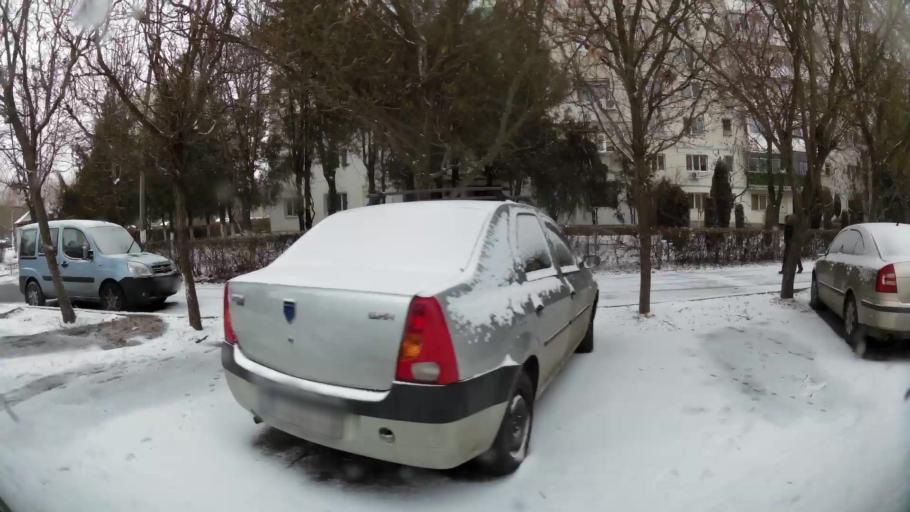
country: RO
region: Prahova
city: Ploiesti
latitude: 44.9316
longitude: 25.9927
